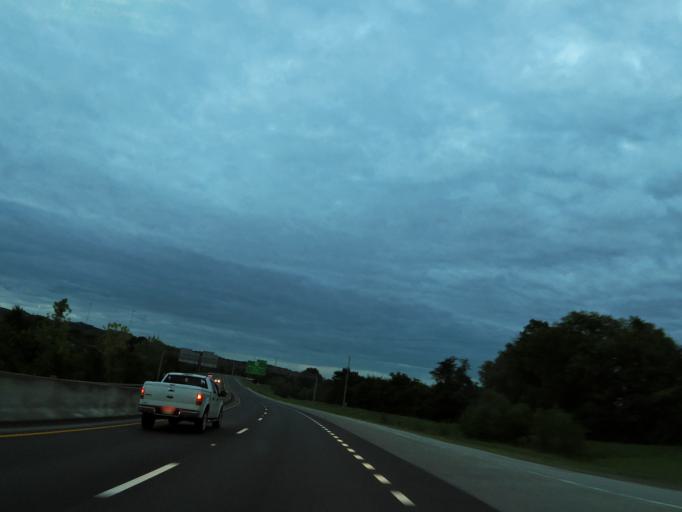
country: US
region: Tennessee
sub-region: Davidson County
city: Nashville
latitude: 36.2295
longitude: -86.8309
